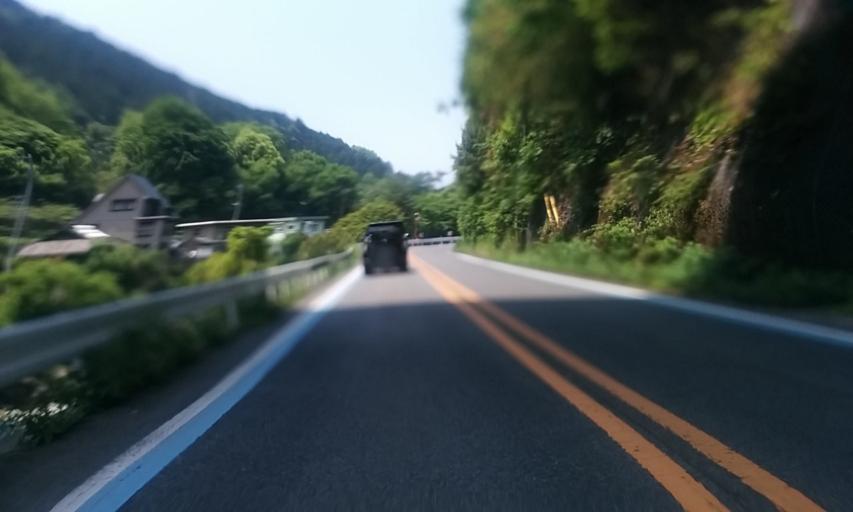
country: JP
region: Ehime
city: Niihama
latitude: 33.9181
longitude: 133.3120
